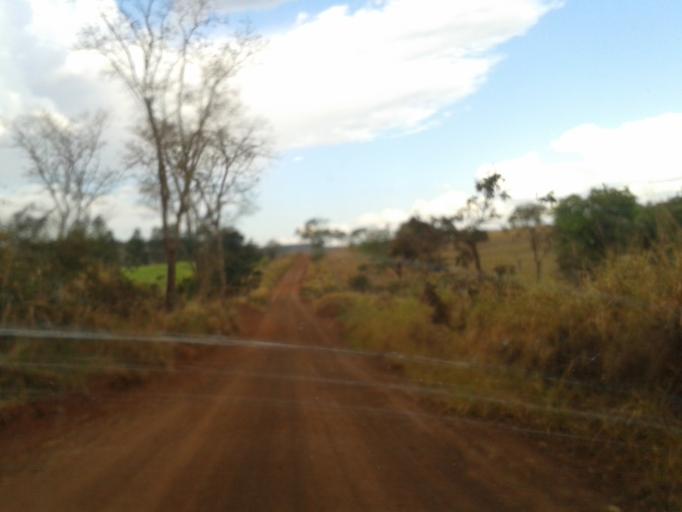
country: BR
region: Minas Gerais
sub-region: Santa Vitoria
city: Santa Vitoria
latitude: -19.2016
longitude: -49.9030
